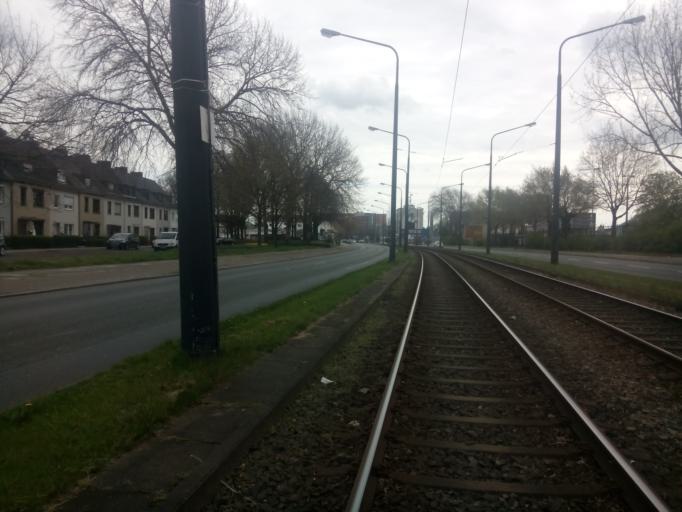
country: DE
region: Bremen
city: Bremen
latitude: 53.0907
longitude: 8.7825
